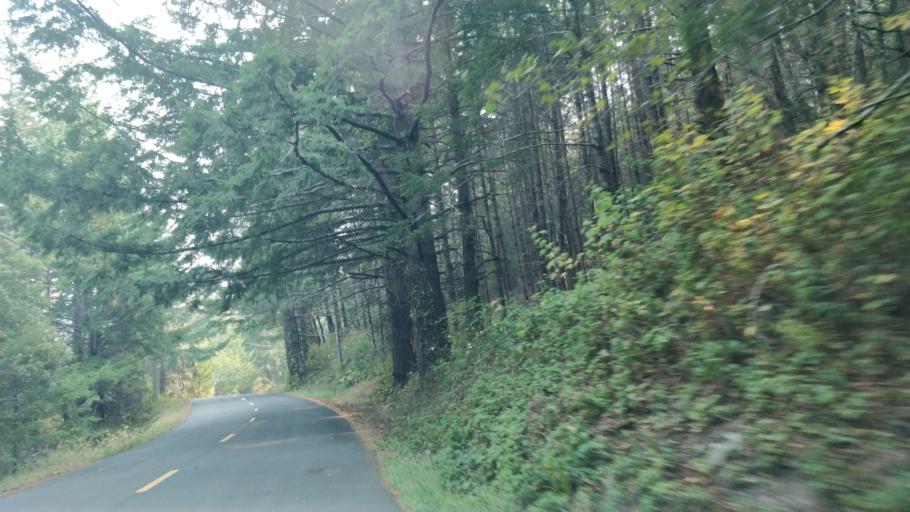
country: US
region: California
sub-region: Humboldt County
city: Rio Dell
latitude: 40.2966
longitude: -124.2506
